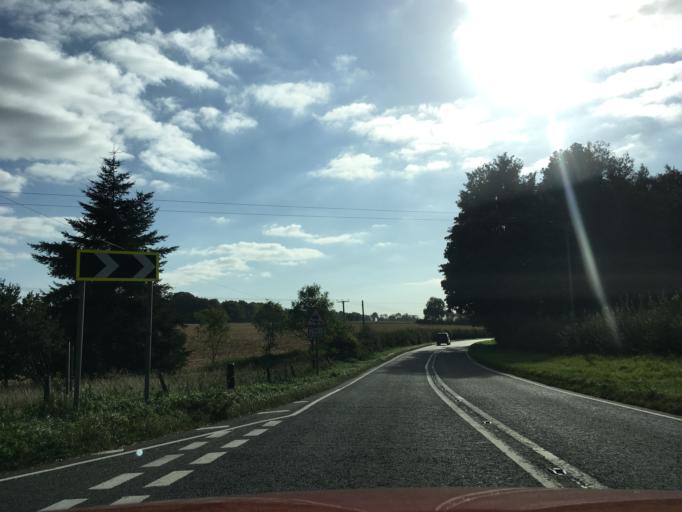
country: GB
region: England
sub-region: Hampshire
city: Old Basing
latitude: 51.1899
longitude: -1.0452
